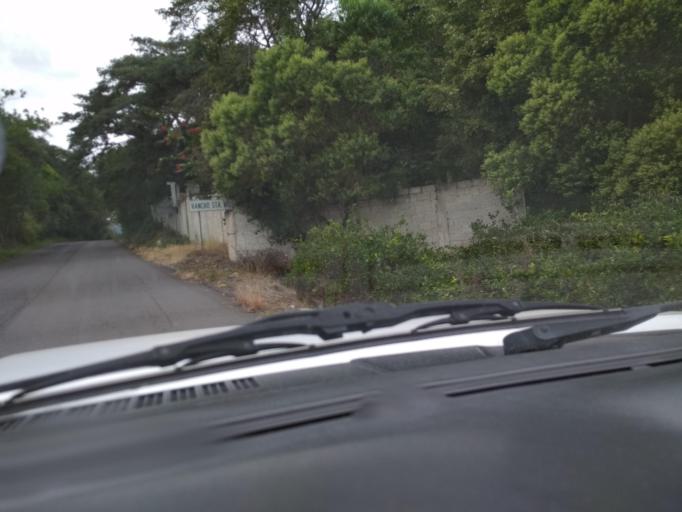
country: MX
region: Veracruz
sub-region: Actopan
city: Trapiche del Rosario
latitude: 19.5866
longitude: -96.7889
